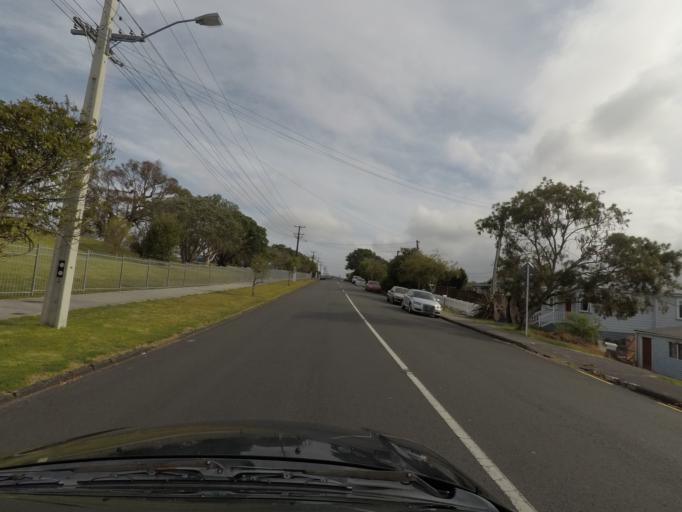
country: NZ
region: Auckland
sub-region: Auckland
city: Waitakere
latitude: -36.9042
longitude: 174.6646
